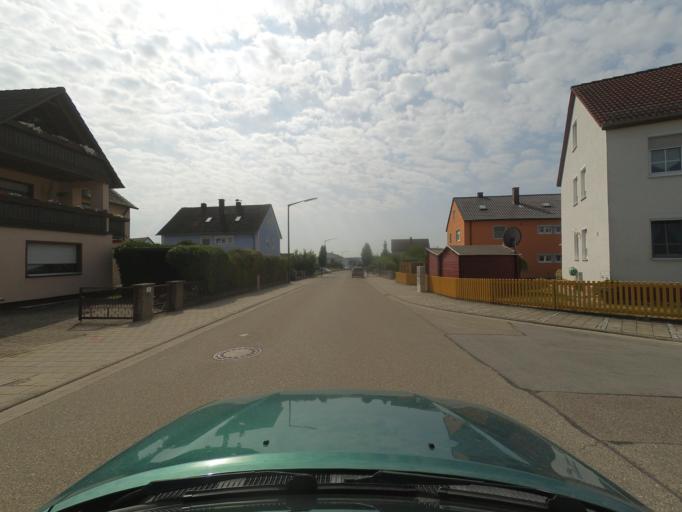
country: DE
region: Bavaria
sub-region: Regierungsbezirk Mittelfranken
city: Arberg
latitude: 49.1650
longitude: 10.5539
